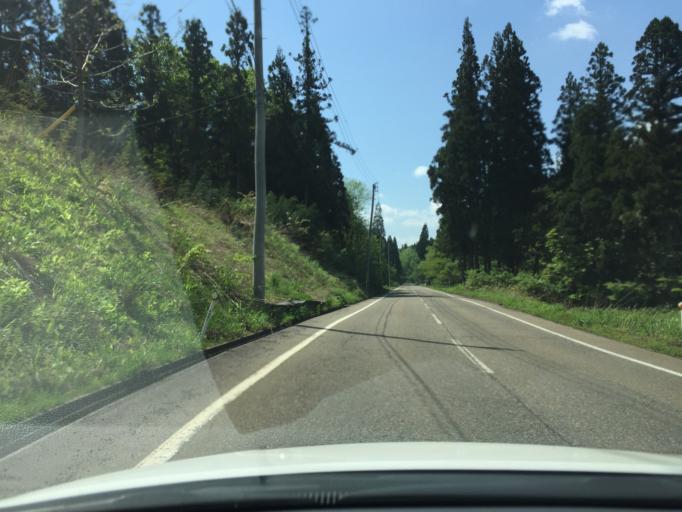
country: JP
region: Niigata
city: Tochio-honcho
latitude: 37.5304
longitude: 139.0949
